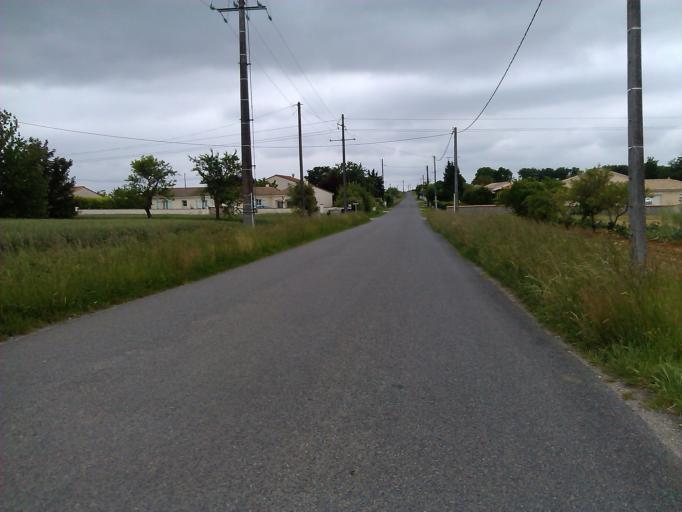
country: FR
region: Poitou-Charentes
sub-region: Departement de la Charente
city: Chateauneuf-sur-Charente
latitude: 45.5862
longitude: -0.0549
